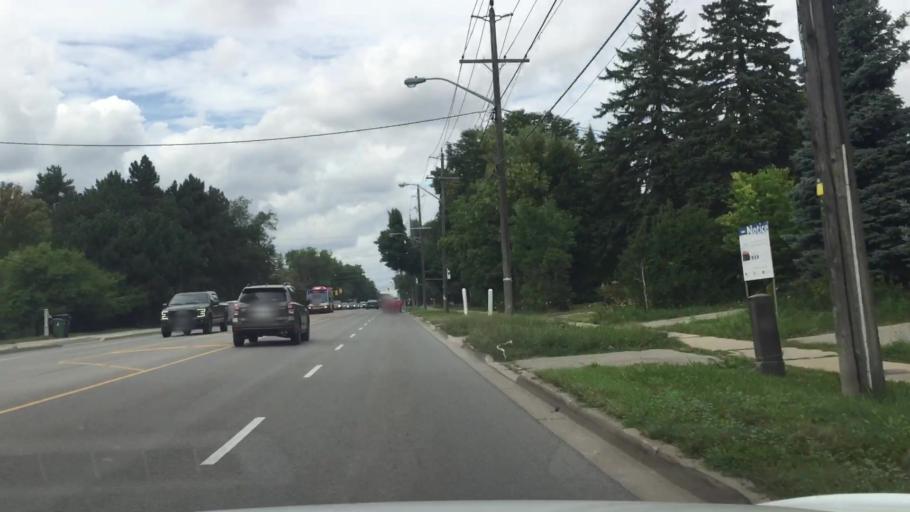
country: CA
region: Ontario
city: Willowdale
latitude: 43.7525
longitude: -79.3850
